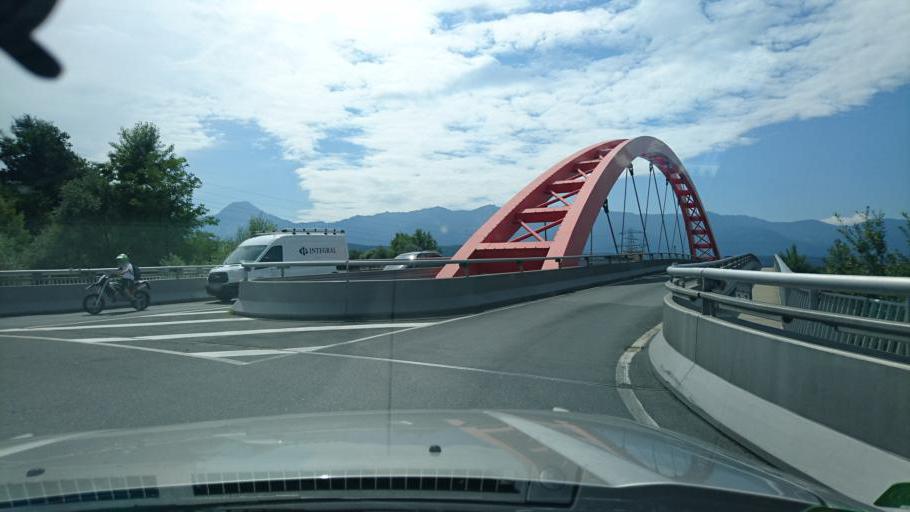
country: AT
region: Carinthia
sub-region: Villach Stadt
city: Villach
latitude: 46.6163
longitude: 13.8789
